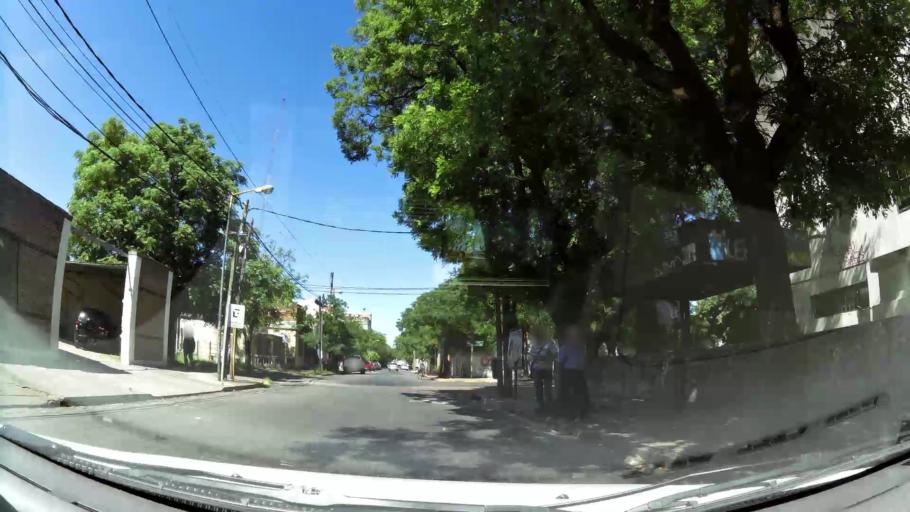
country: AR
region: Buenos Aires
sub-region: Partido de General San Martin
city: General San Martin
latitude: -34.5815
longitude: -58.5440
